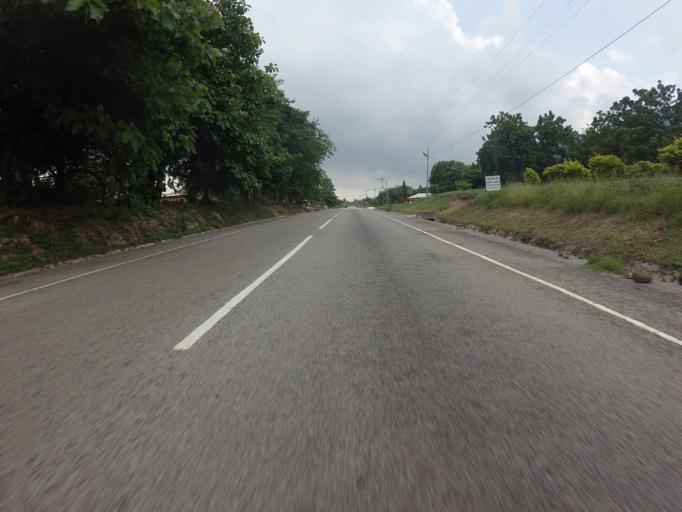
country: GH
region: Volta
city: Ho
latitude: 6.7644
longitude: 0.4802
